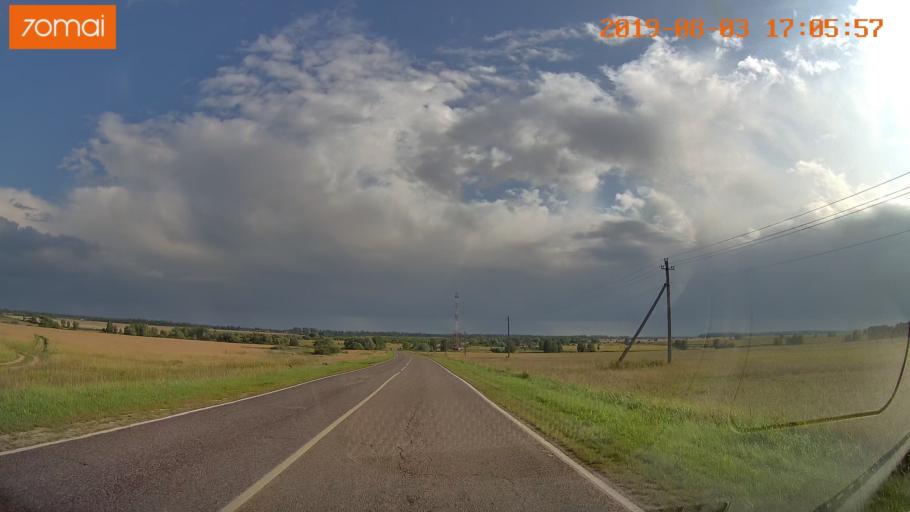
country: RU
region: Moskovskaya
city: Troitskoye
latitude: 55.3152
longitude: 38.5512
